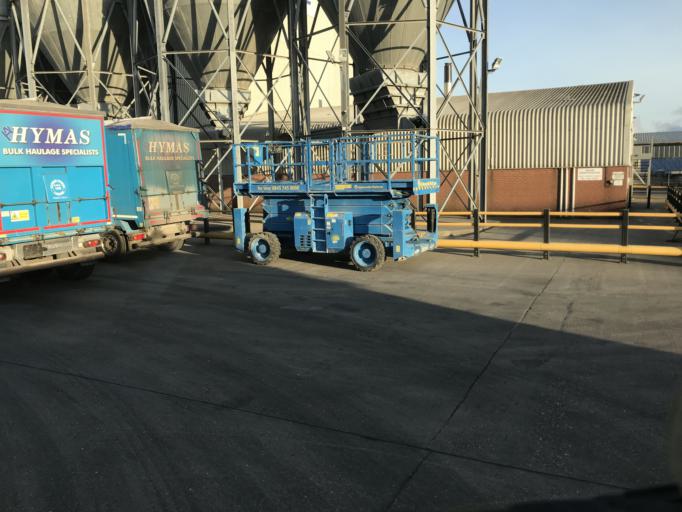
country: GB
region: England
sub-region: North Lincolnshire
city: Burton upon Stather
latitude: 53.6209
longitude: -0.7019
